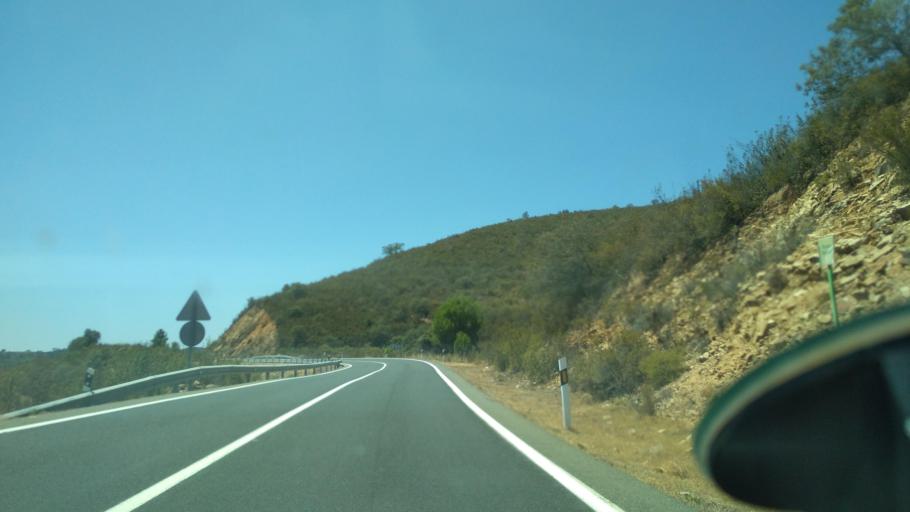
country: ES
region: Andalusia
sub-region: Provincia de Huelva
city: Aracena
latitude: 37.8567
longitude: -6.5621
